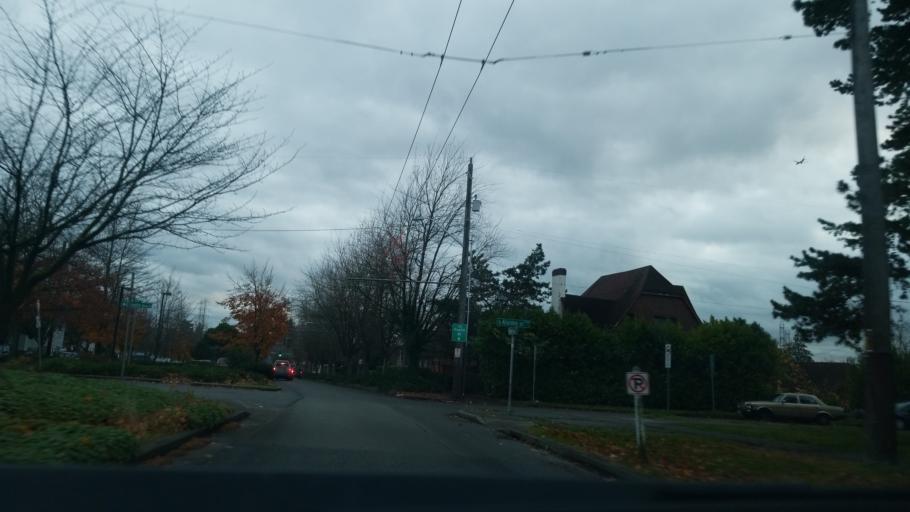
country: US
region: Washington
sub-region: King County
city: Seattle
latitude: 47.5615
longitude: -122.3052
